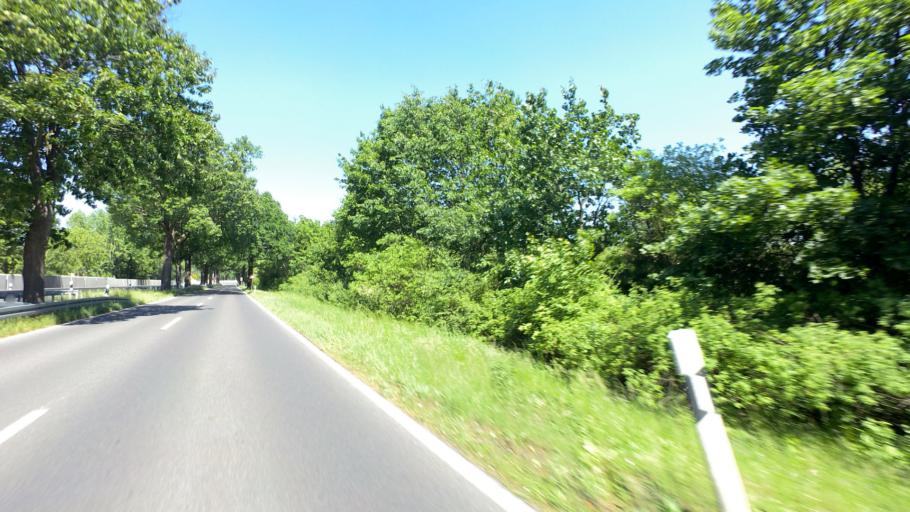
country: DE
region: Brandenburg
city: Peitz
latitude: 51.8029
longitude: 14.3830
